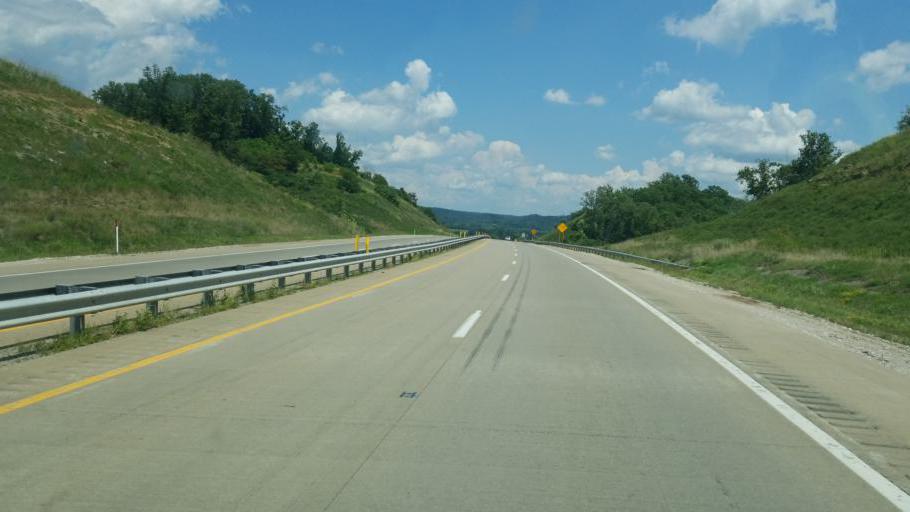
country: US
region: West Virginia
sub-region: Mason County
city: Point Pleasant
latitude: 38.7641
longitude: -82.0175
